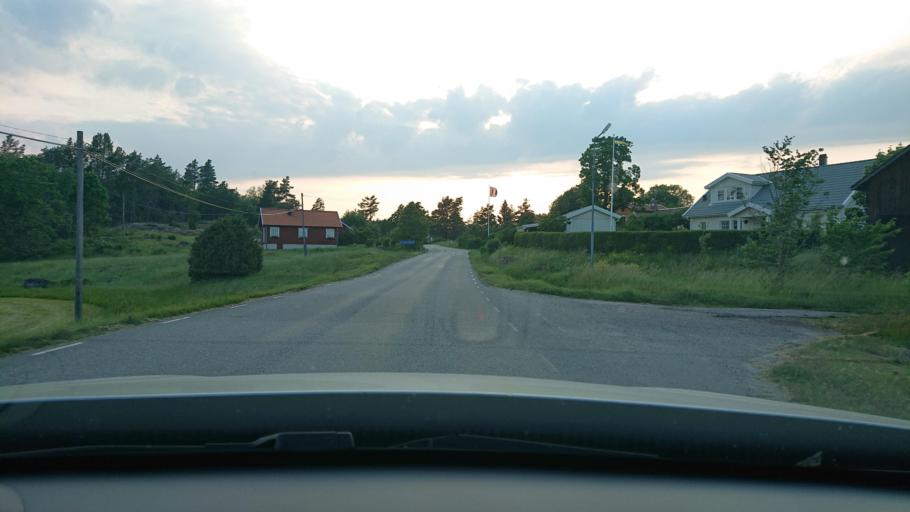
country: SE
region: Stockholm
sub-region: Osterakers Kommun
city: Akersberga
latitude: 59.5085
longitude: 18.3126
